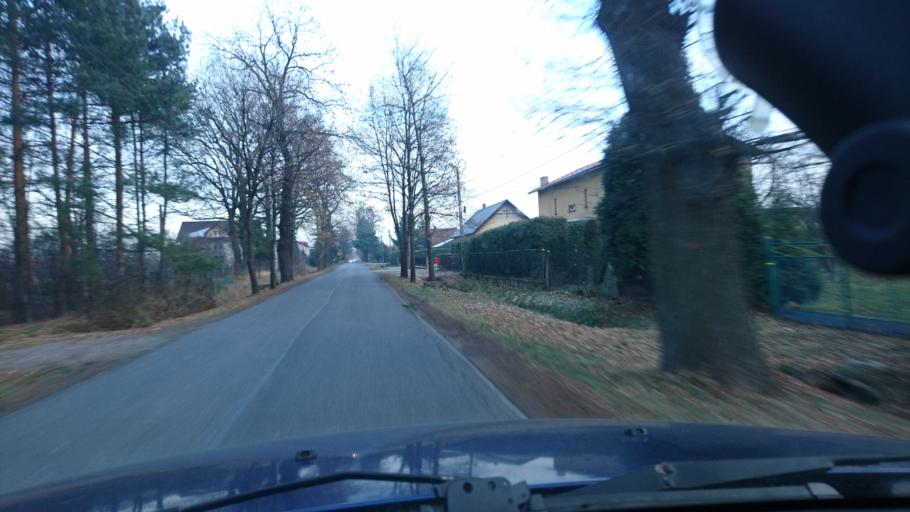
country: PL
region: Silesian Voivodeship
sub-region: Powiat bielski
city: Bestwinka
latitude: 49.9336
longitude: 19.0605
